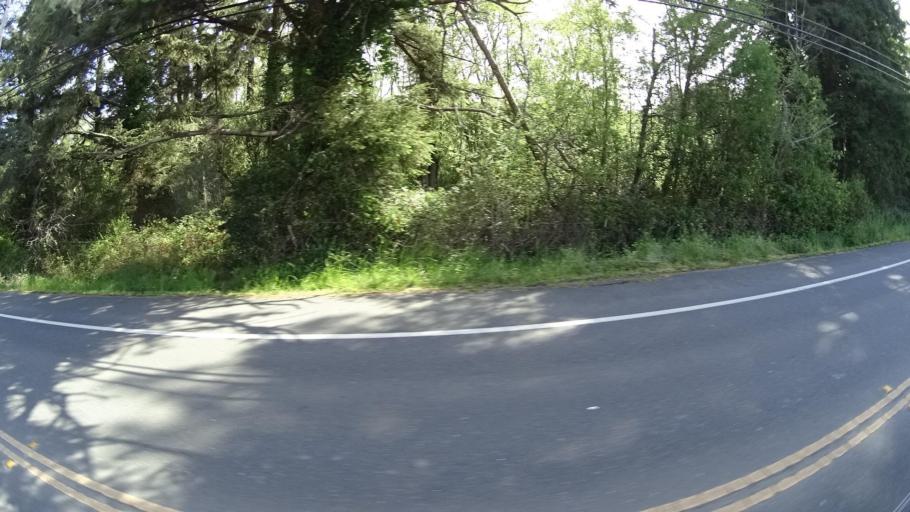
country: US
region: California
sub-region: Humboldt County
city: Myrtletown
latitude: 40.7916
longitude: -124.0866
